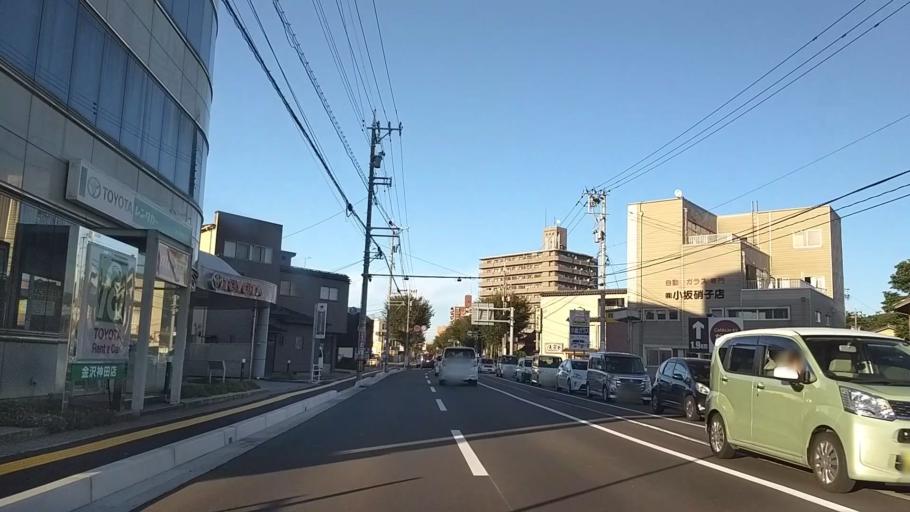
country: JP
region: Ishikawa
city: Nonoichi
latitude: 36.5593
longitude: 136.6381
